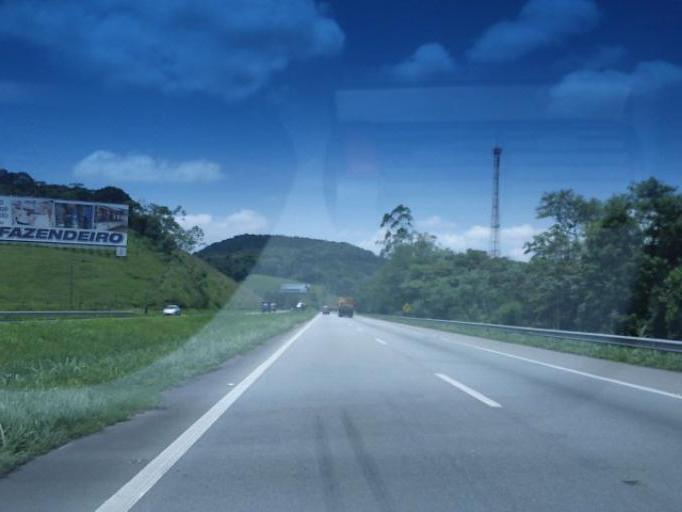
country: BR
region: Sao Paulo
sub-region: Miracatu
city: Miracatu
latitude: -24.2167
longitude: -47.3672
